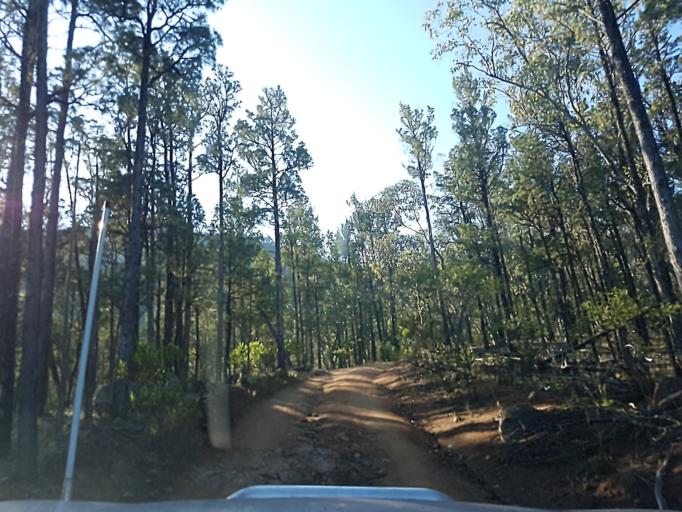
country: AU
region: New South Wales
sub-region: Snowy River
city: Jindabyne
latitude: -36.9497
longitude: 148.3804
